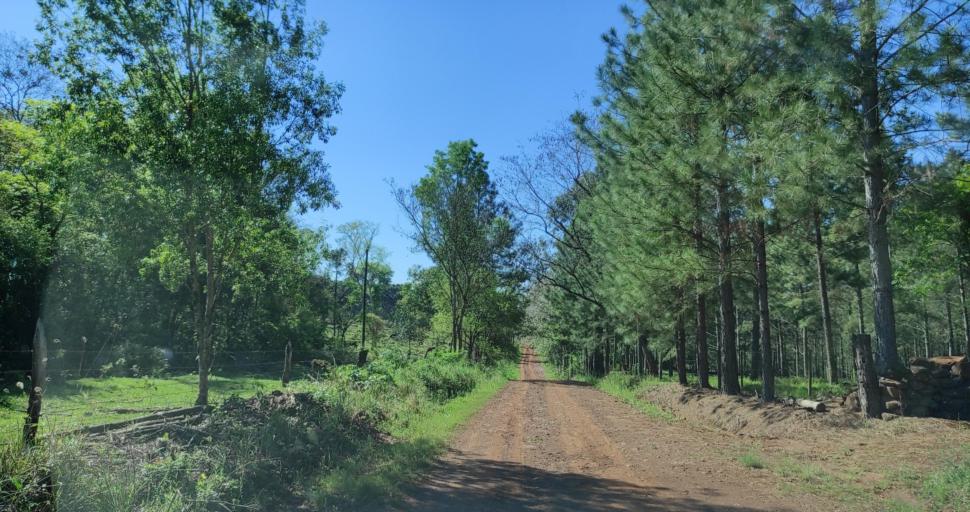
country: AR
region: Misiones
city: Capiovi
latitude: -26.9376
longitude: -55.0019
